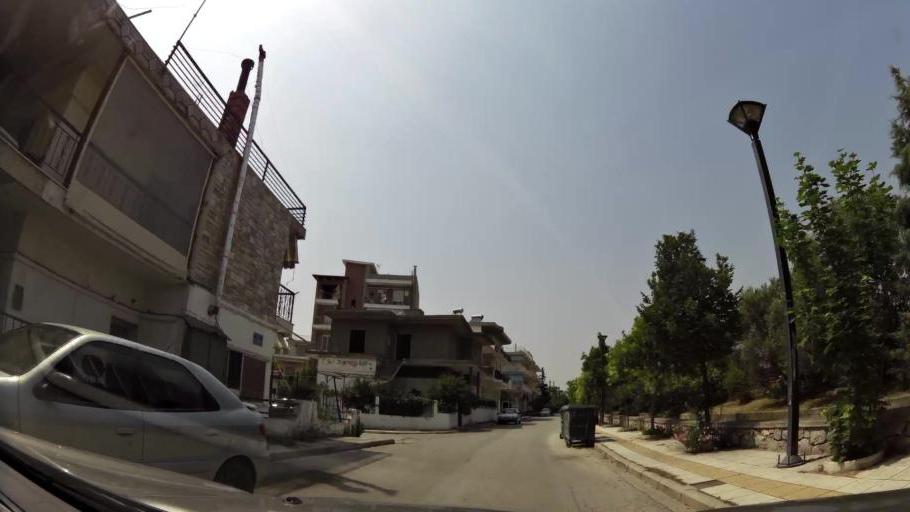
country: GR
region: Central Macedonia
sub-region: Nomos Thessalonikis
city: Diavata
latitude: 40.6881
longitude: 22.8624
